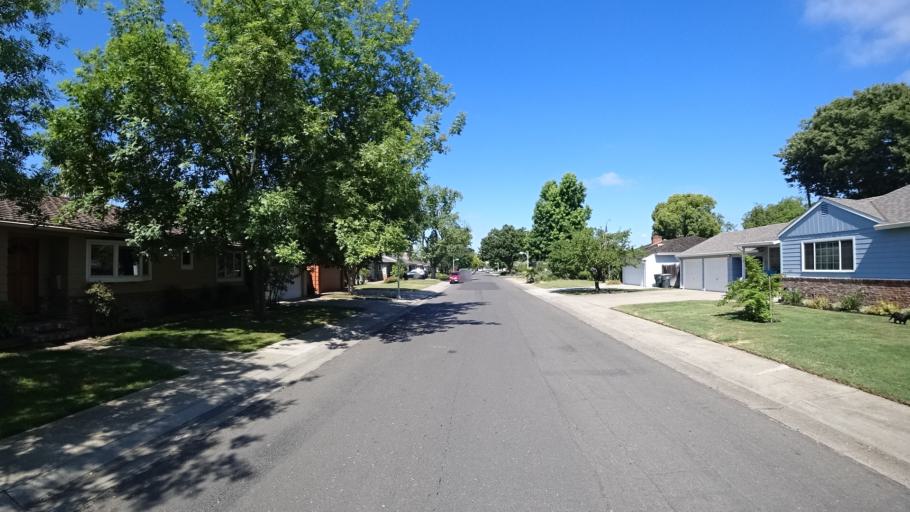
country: US
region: California
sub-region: Sacramento County
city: Parkway
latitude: 38.5323
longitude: -121.4914
